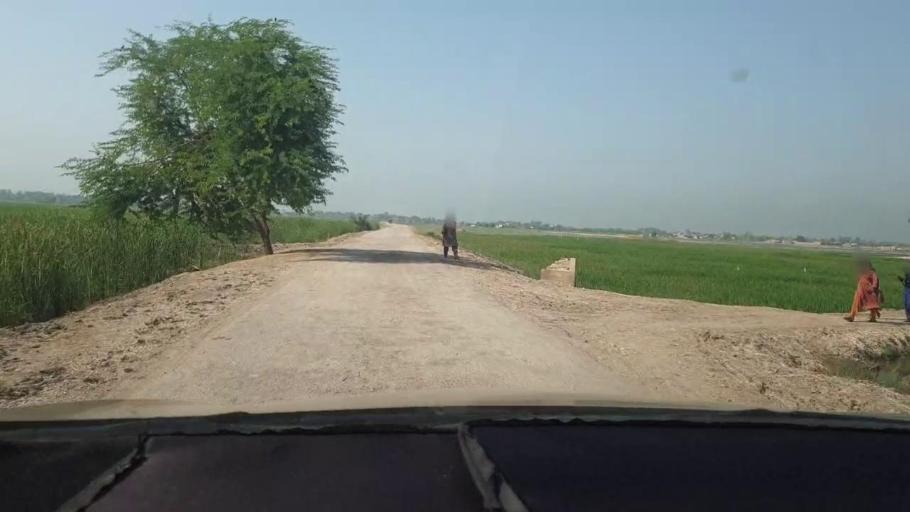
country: PK
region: Sindh
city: Kambar
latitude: 27.5795
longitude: 68.0906
